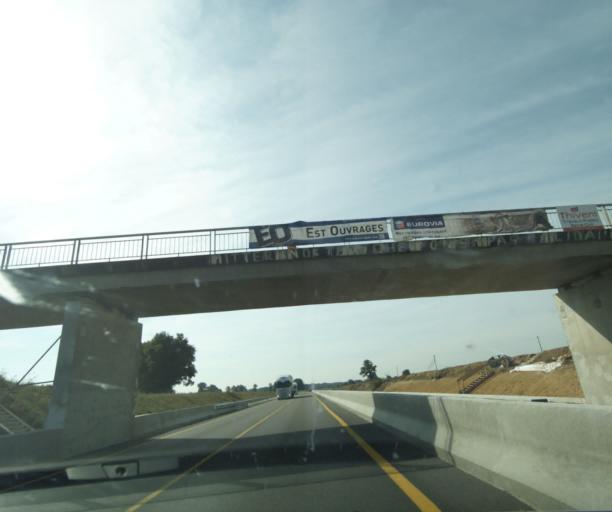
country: FR
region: Bourgogne
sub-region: Departement de Saone-et-Loire
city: Paray-le-Monial
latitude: 46.5054
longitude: 4.1611
